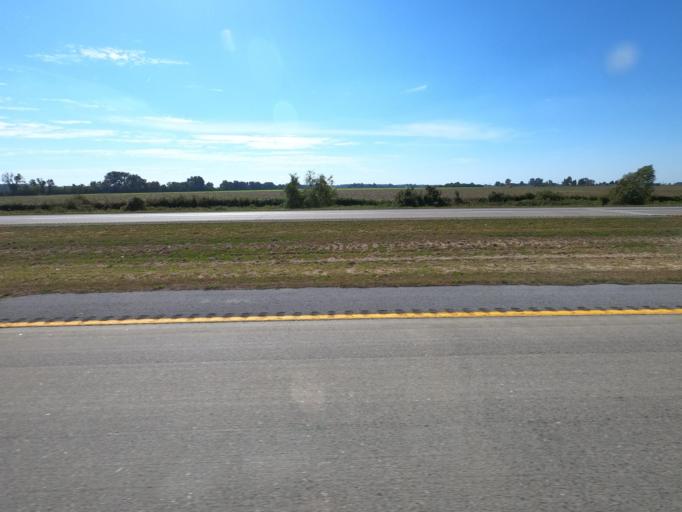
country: US
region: Missouri
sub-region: Pemiscot County
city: Caruthersville
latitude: 36.1395
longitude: -89.6359
